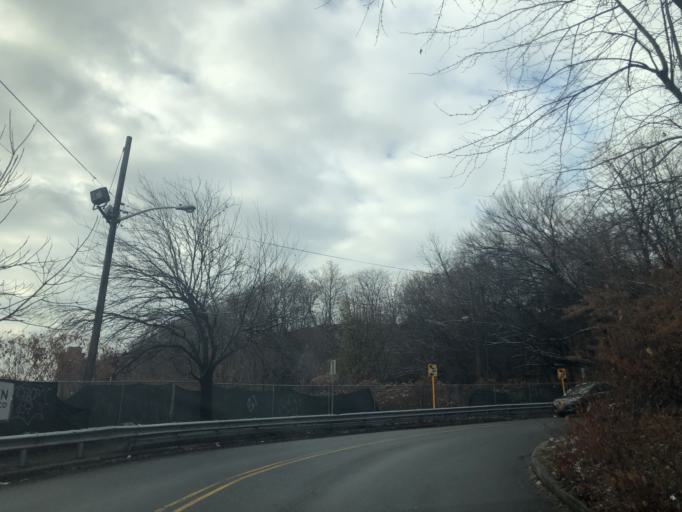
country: US
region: New Jersey
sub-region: Hudson County
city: Hoboken
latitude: 40.7375
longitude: -74.0467
